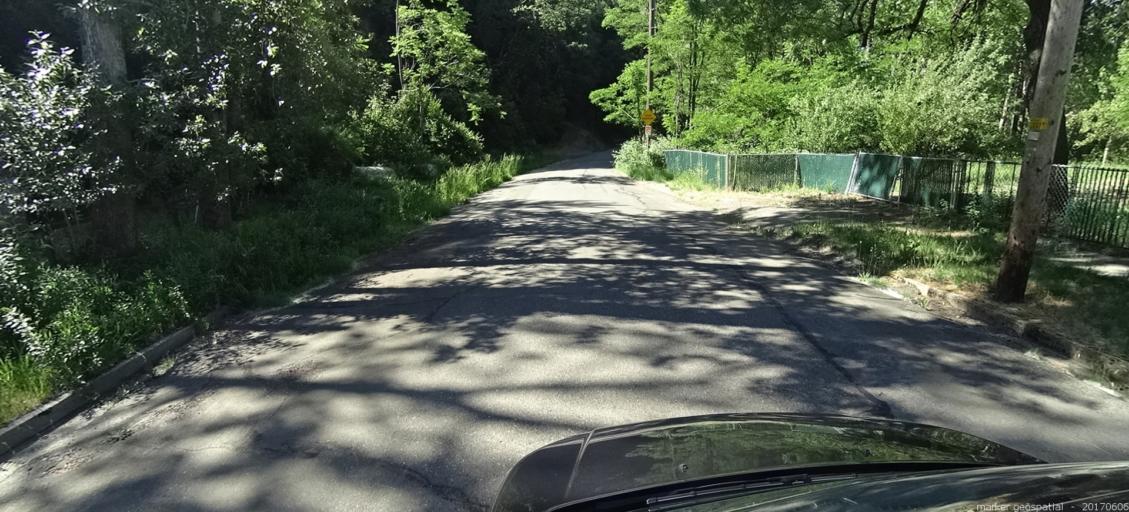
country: US
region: California
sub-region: Siskiyou County
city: Dunsmuir
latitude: 41.2056
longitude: -122.2704
